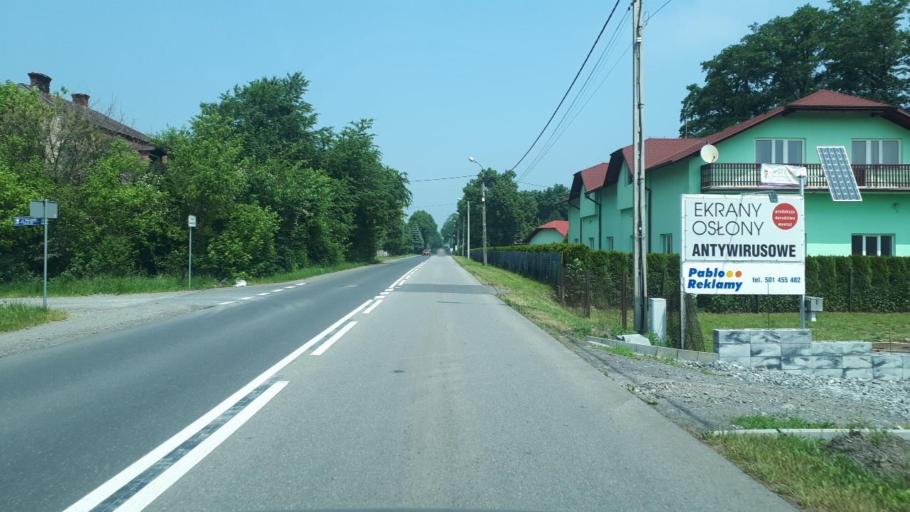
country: PL
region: Silesian Voivodeship
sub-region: Powiat cieszynski
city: Ustron
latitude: 49.7481
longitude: 18.8045
